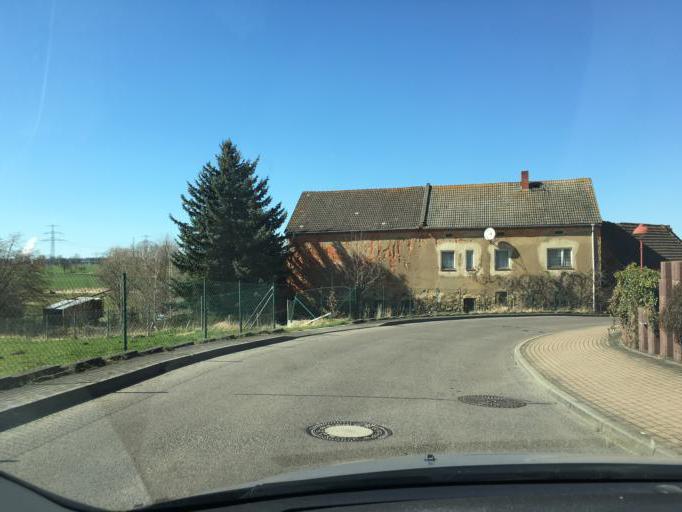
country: DE
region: Saxony
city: Kitzscher
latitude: 51.1512
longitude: 12.5357
